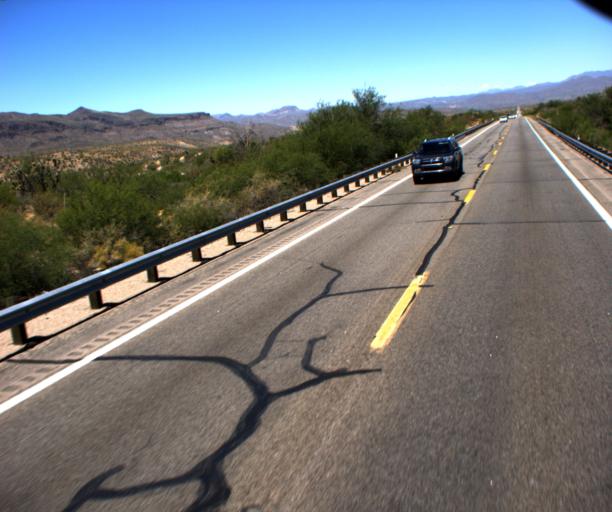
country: US
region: Arizona
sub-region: Yavapai County
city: Bagdad
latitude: 34.3034
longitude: -113.1209
